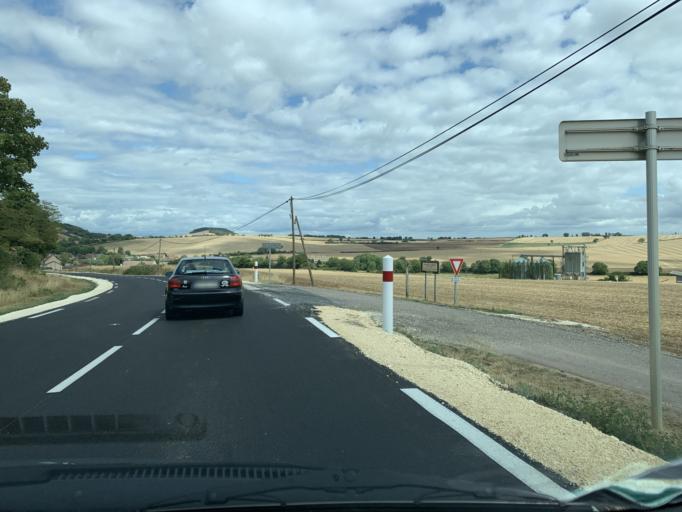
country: FR
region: Bourgogne
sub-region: Departement de la Nievre
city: Varzy
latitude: 47.3501
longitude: 3.3780
